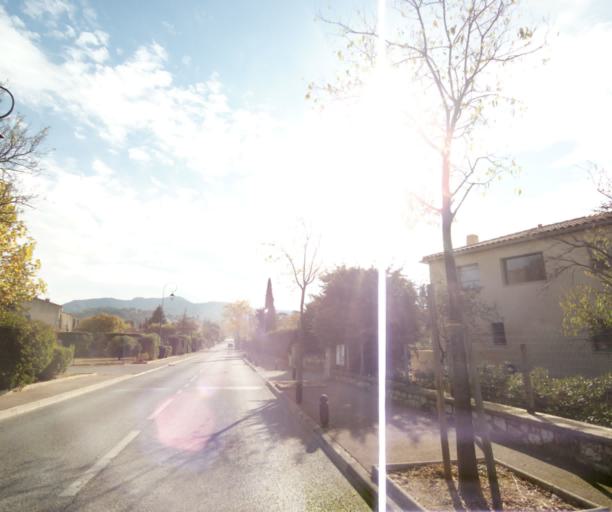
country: FR
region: Provence-Alpes-Cote d'Azur
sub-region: Departement des Bouches-du-Rhone
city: Gemenos
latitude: 43.3002
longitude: 5.6196
